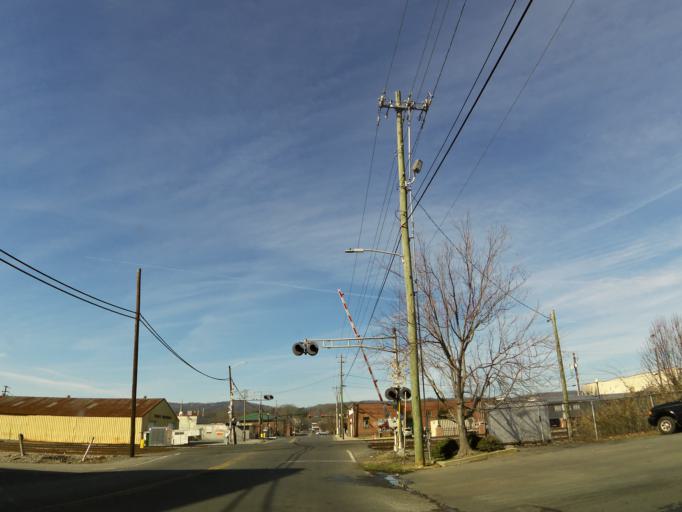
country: US
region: Georgia
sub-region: Whitfield County
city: Dalton
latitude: 34.7687
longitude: -84.9660
